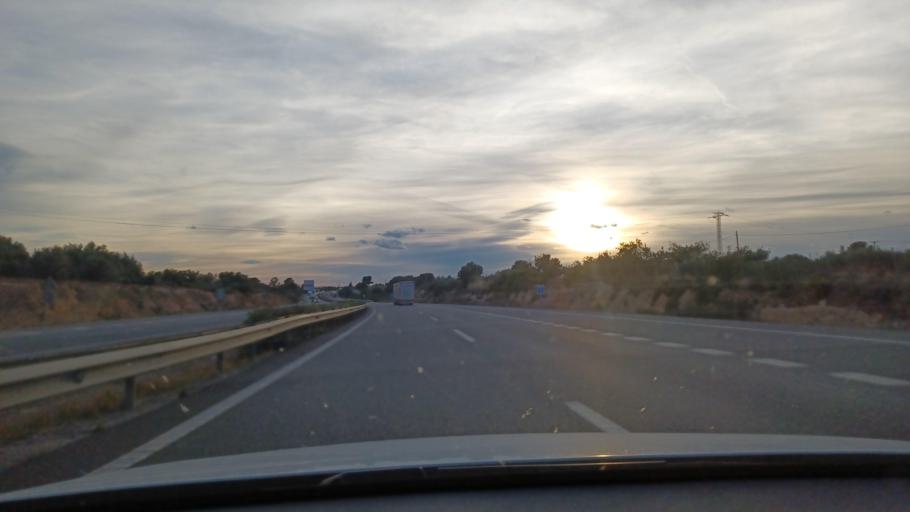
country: ES
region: Catalonia
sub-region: Provincia de Tarragona
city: L'Ampolla
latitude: 40.8103
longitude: 0.7010
